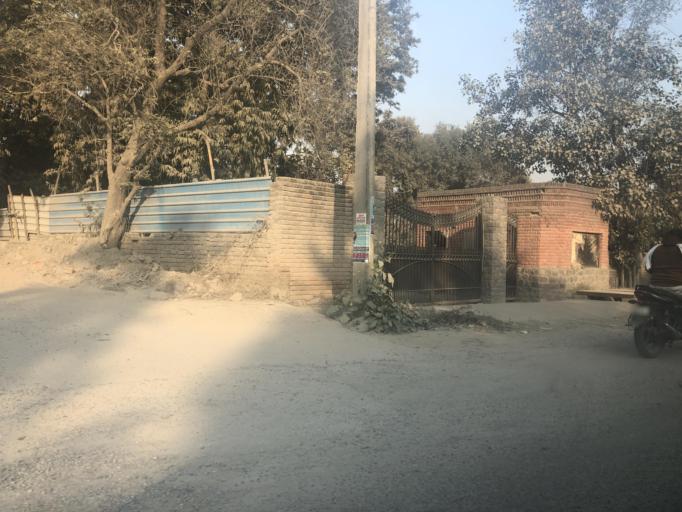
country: IN
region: Haryana
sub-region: Gurgaon
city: Gurgaon
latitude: 28.5400
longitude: 77.0270
